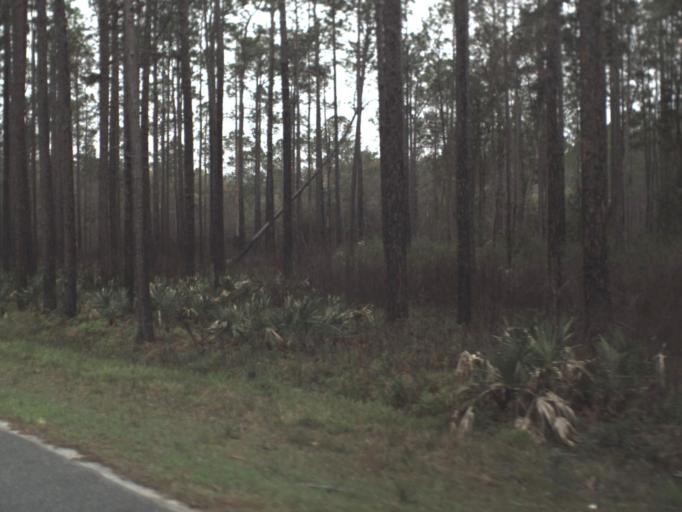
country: US
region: Florida
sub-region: Franklin County
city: Apalachicola
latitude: 29.9371
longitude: -84.9768
